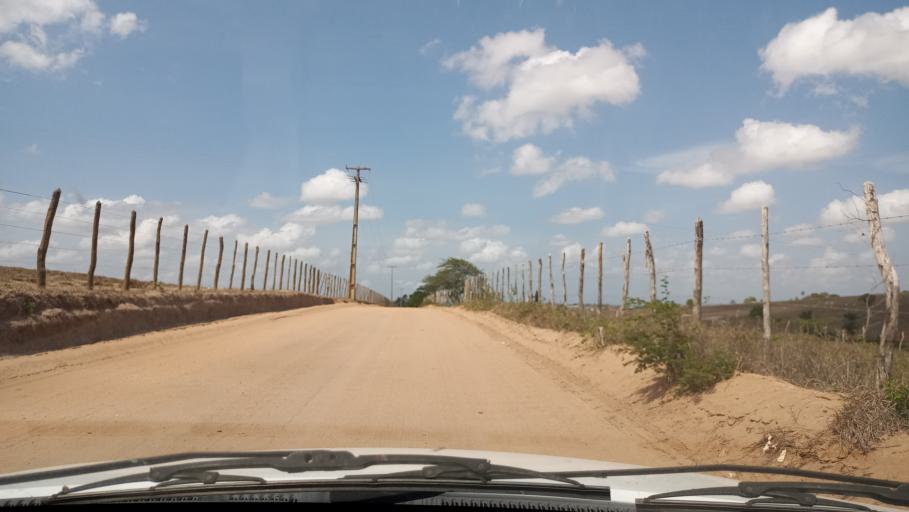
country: BR
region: Rio Grande do Norte
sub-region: Goianinha
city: Goianinha
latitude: -6.3441
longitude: -35.3280
